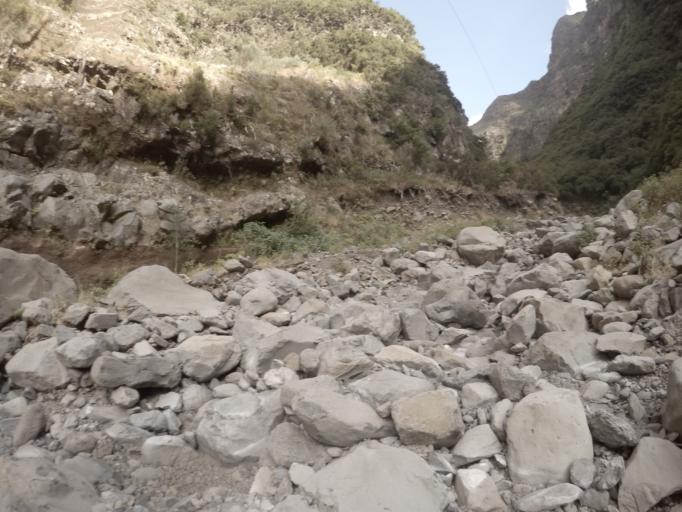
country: PT
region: Madeira
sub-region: Funchal
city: Nossa Senhora do Monte
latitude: 32.7011
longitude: -16.9204
